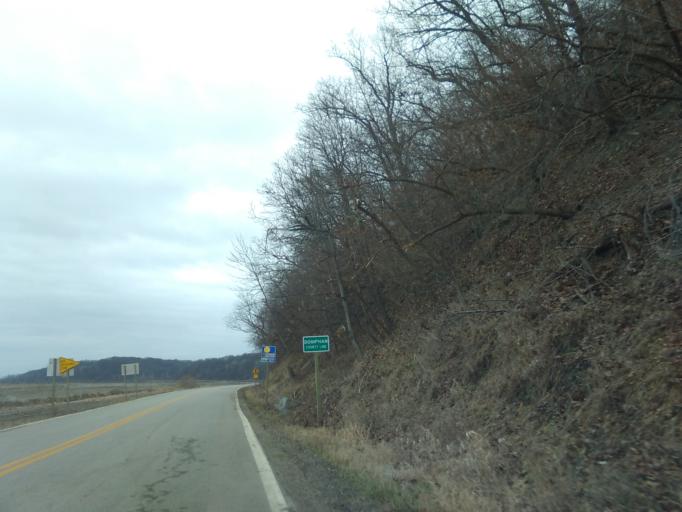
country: US
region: Kansas
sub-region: Doniphan County
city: Highland
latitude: 39.9999
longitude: -95.3313
